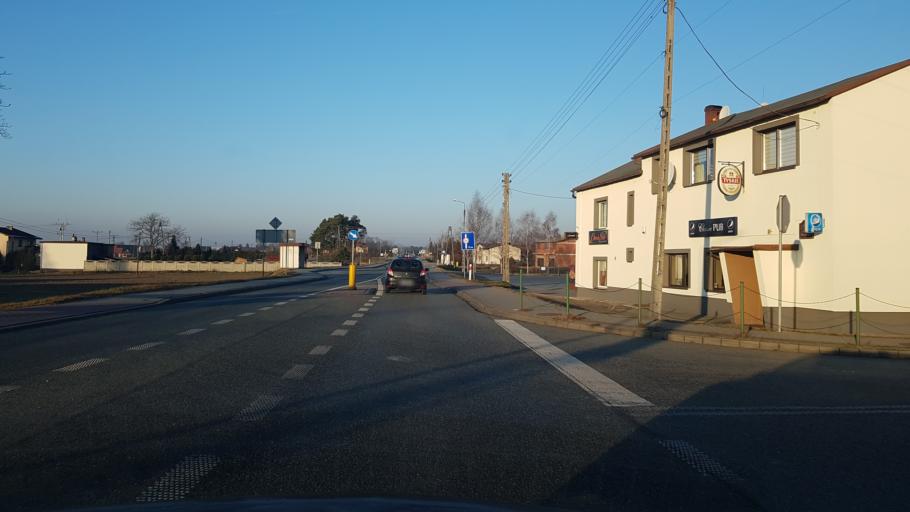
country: PL
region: Silesian Voivodeship
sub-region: Powiat pszczynski
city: Rudziczka
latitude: 50.0364
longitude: 18.7556
